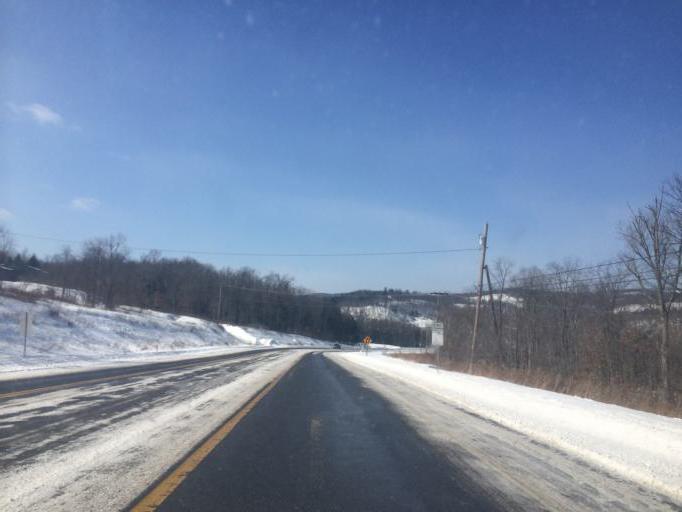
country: US
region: Pennsylvania
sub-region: Centre County
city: Stormstown
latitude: 40.8275
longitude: -78.0086
